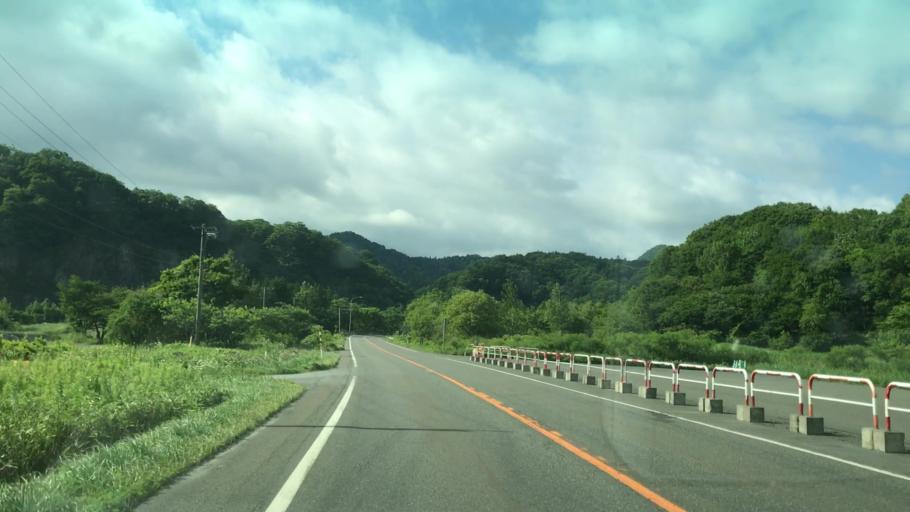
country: JP
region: Hokkaido
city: Shizunai-furukawacho
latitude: 42.7913
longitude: 142.3943
